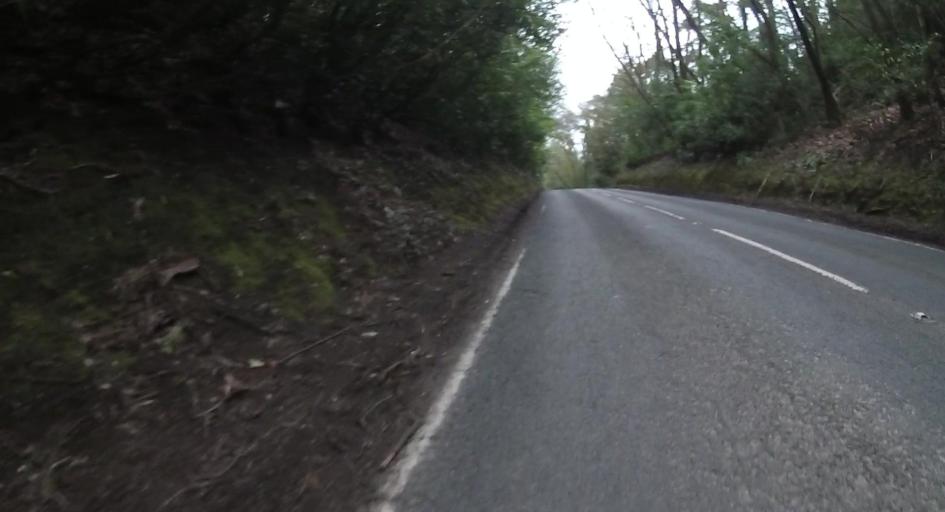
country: GB
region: England
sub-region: Surrey
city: Farnham
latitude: 51.1842
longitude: -0.7910
